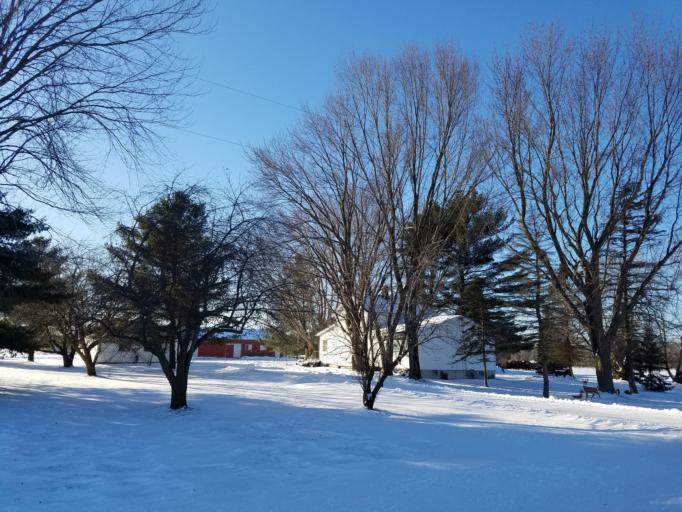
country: US
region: Wisconsin
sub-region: Marathon County
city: Spencer
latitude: 44.6706
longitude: -90.3420
